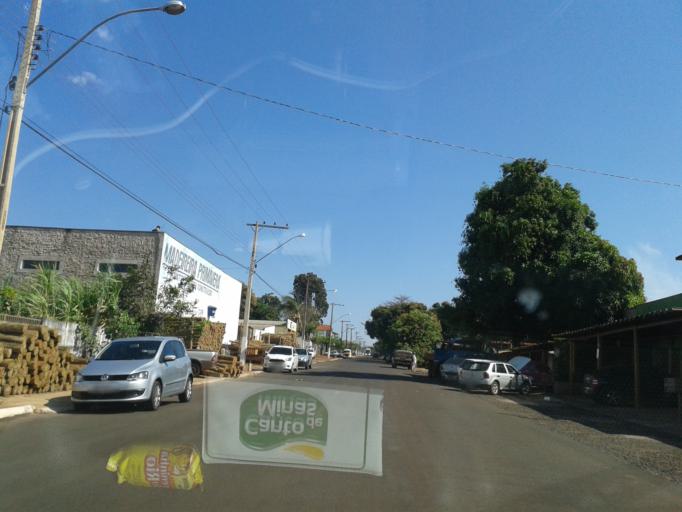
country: BR
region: Minas Gerais
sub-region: Santa Vitoria
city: Santa Vitoria
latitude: -19.0036
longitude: -50.5511
